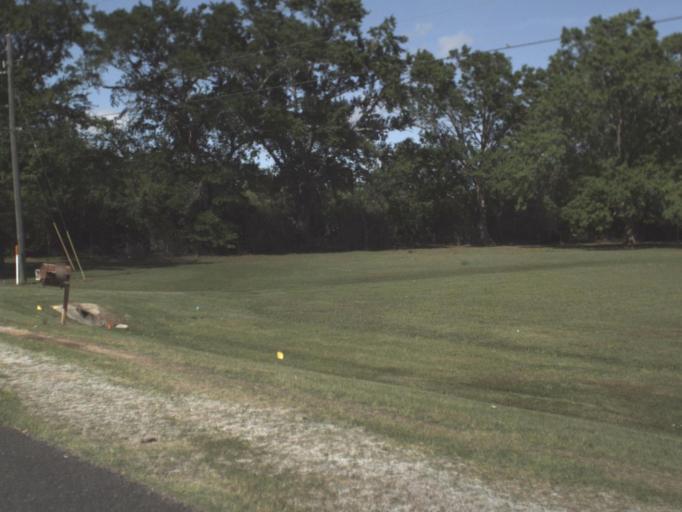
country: US
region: Florida
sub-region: Escambia County
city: Molino
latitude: 30.7089
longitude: -87.3500
